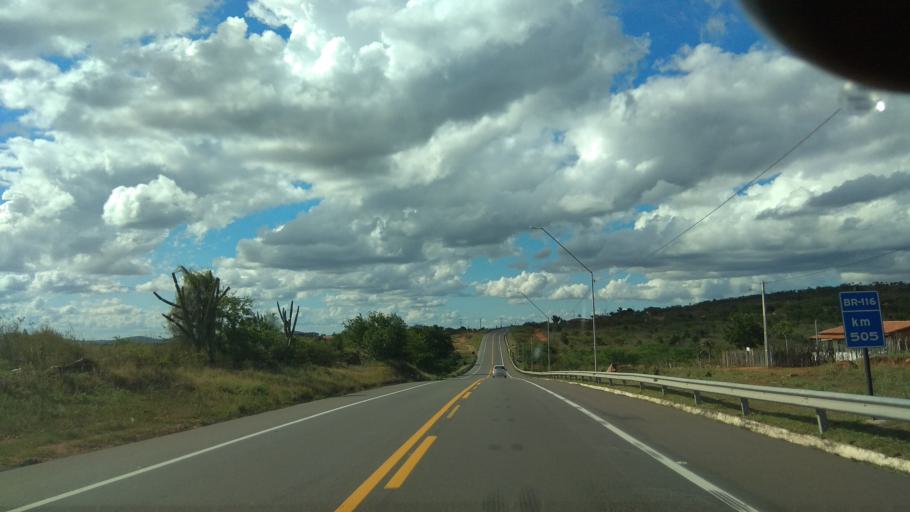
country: BR
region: Bahia
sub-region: Castro Alves
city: Castro Alves
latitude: -12.6309
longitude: -39.5973
